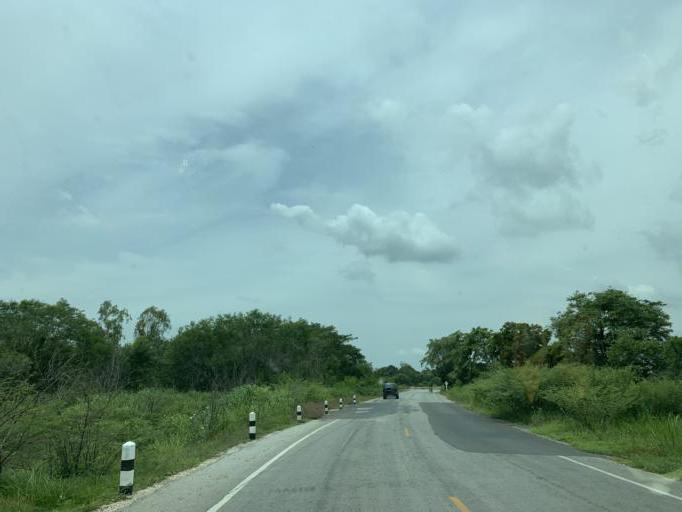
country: TH
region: Uthai Thani
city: Uthai Thani
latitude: 15.4051
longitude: 100.0255
